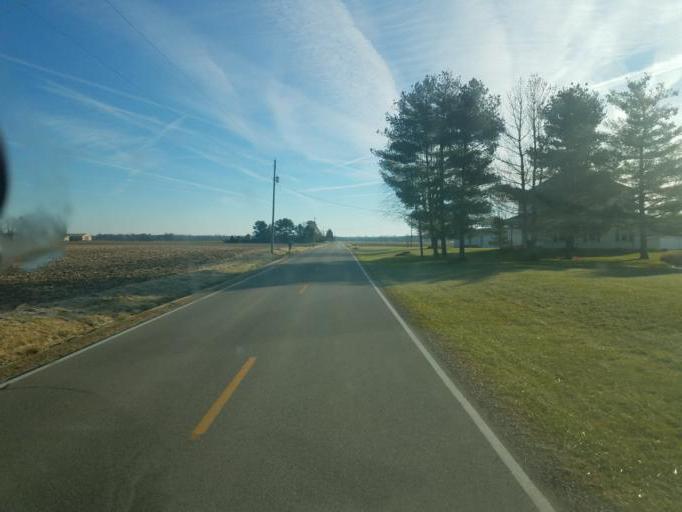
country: US
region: Ohio
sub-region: Crawford County
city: Galion
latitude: 40.7332
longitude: -82.8844
